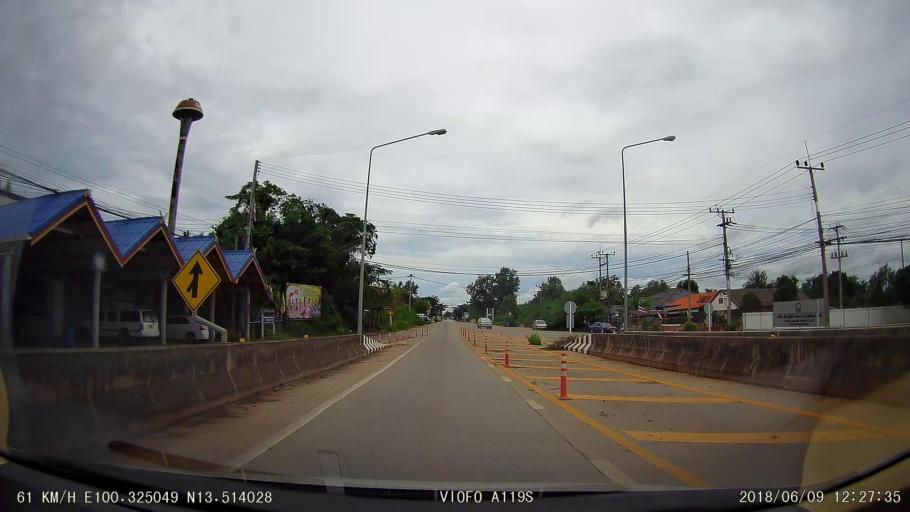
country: TH
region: Samut Sakhon
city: Samut Sakhon
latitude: 13.5140
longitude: 100.3251
